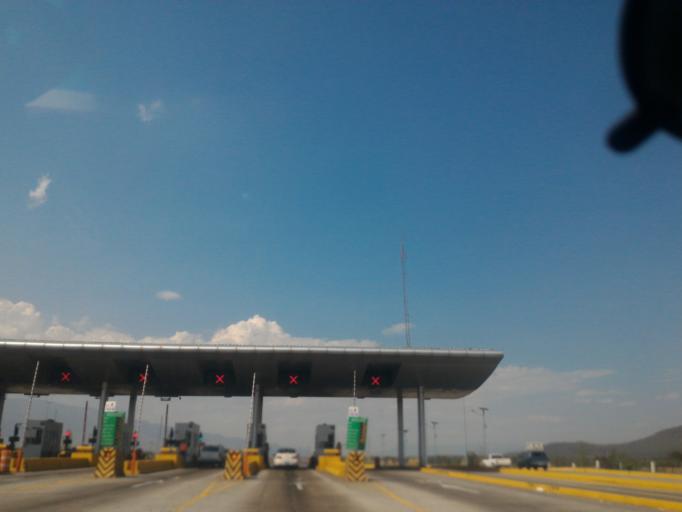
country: MX
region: Jalisco
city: Usmajac
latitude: 19.9328
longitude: -103.5297
